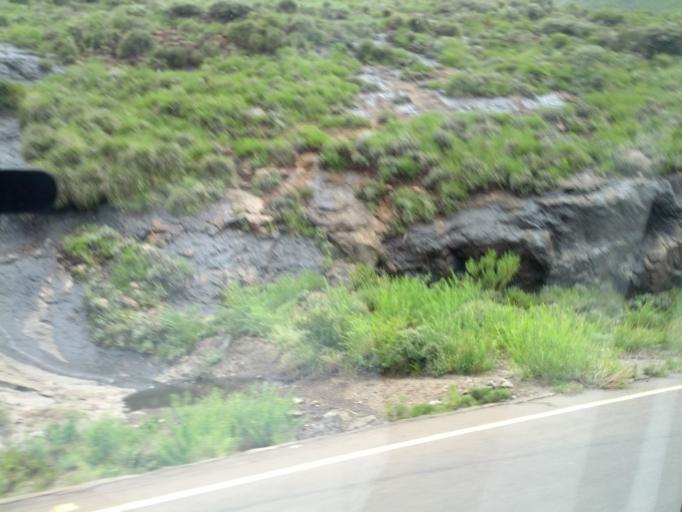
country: LS
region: Butha-Buthe
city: Butha-Buthe
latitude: -29.0602
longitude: 28.3584
